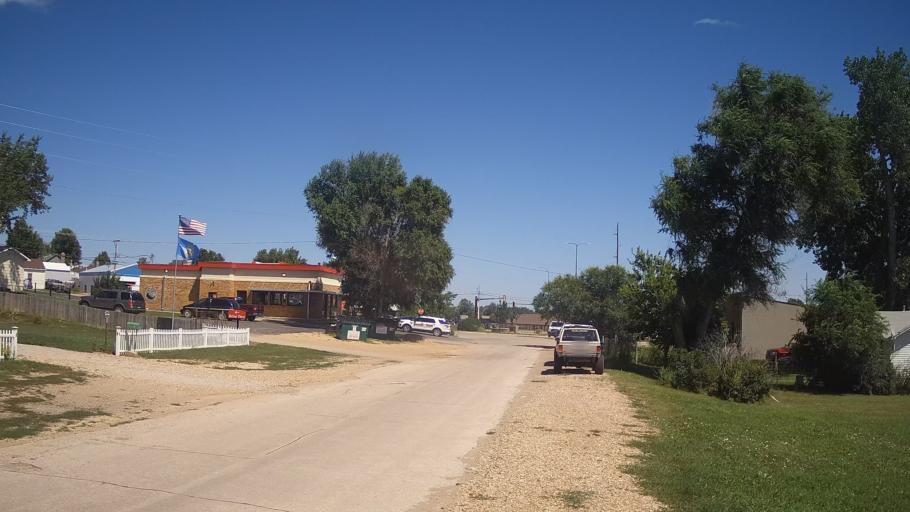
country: US
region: South Dakota
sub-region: Butte County
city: Belle Fourche
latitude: 44.6617
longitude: -103.8559
